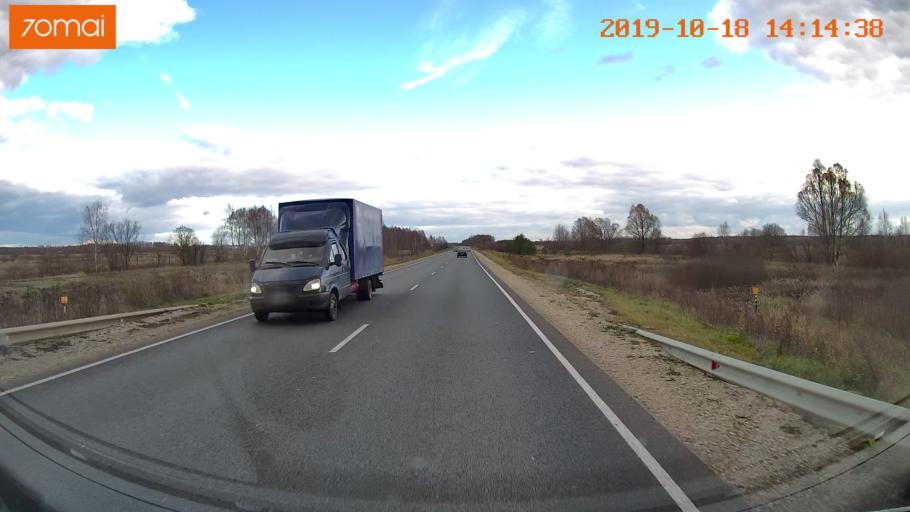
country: RU
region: Rjazan
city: Spas-Klepiki
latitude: 55.1497
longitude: 40.2994
